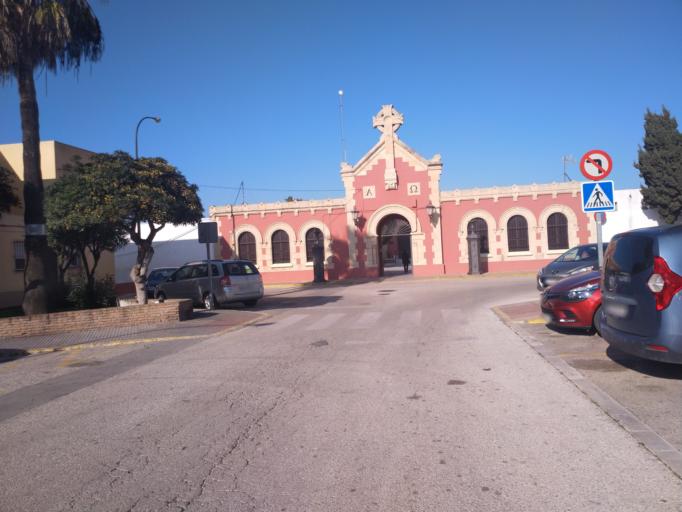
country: ES
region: Andalusia
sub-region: Provincia de Cadiz
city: San Fernando
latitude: 36.4688
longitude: -6.2031
